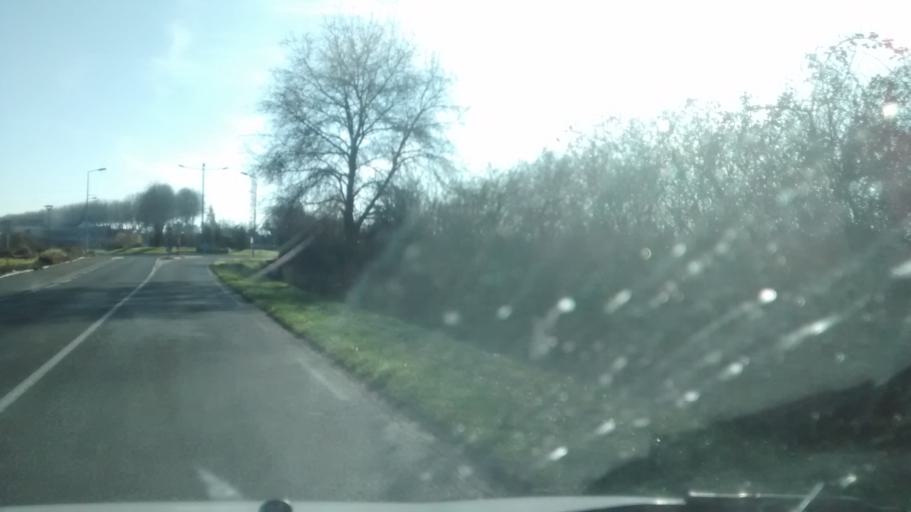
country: FR
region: Centre
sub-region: Departement d'Indre-et-Loire
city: Nazelles-Negron
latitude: 47.4285
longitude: 0.9580
